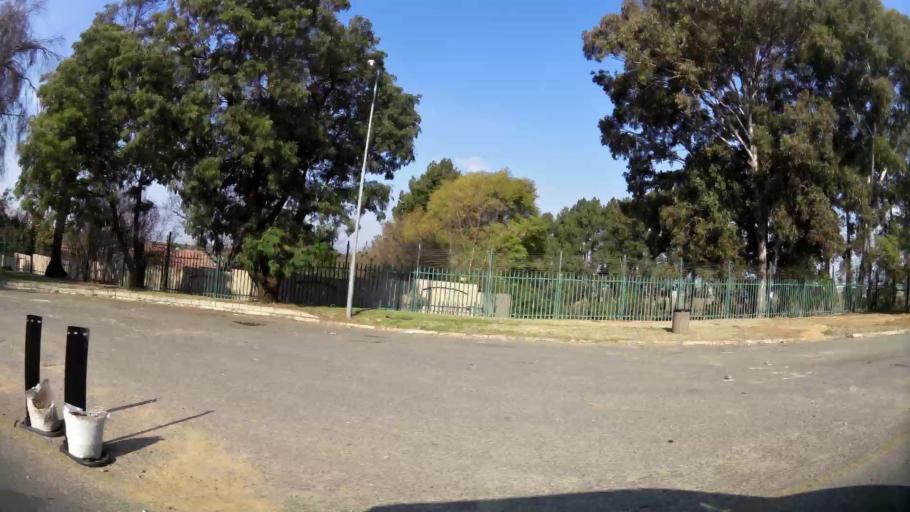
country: ZA
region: Gauteng
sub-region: City of Johannesburg Metropolitan Municipality
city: Modderfontein
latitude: -26.1072
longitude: 28.1485
